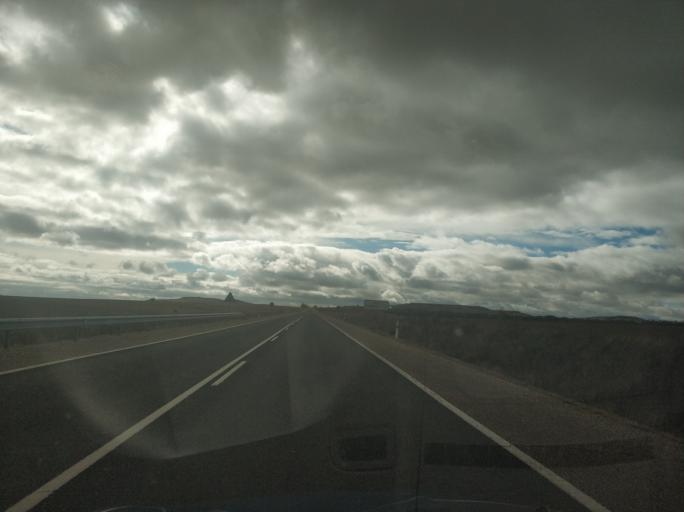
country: ES
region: Castille and Leon
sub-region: Provincia de Zamora
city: Castrillo de la Guarena
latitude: 41.2219
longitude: -5.3156
